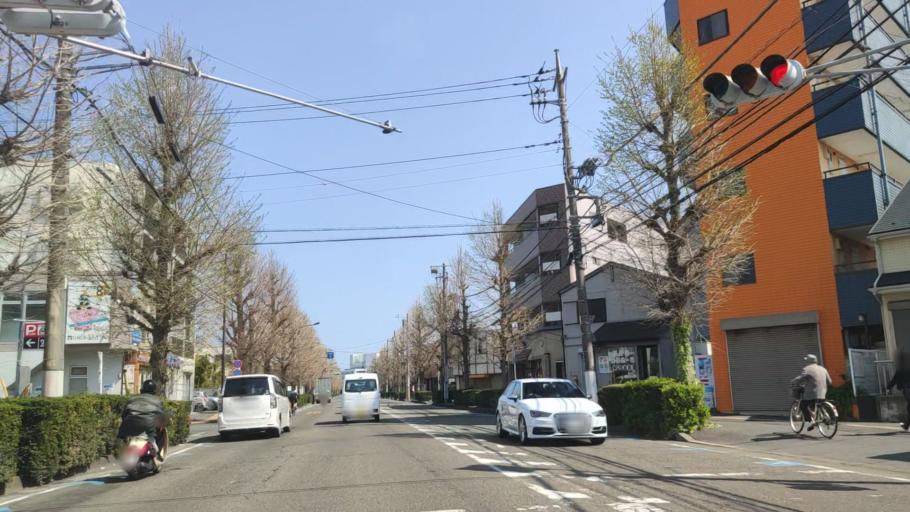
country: JP
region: Kanagawa
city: Hiratsuka
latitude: 35.3361
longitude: 139.3397
